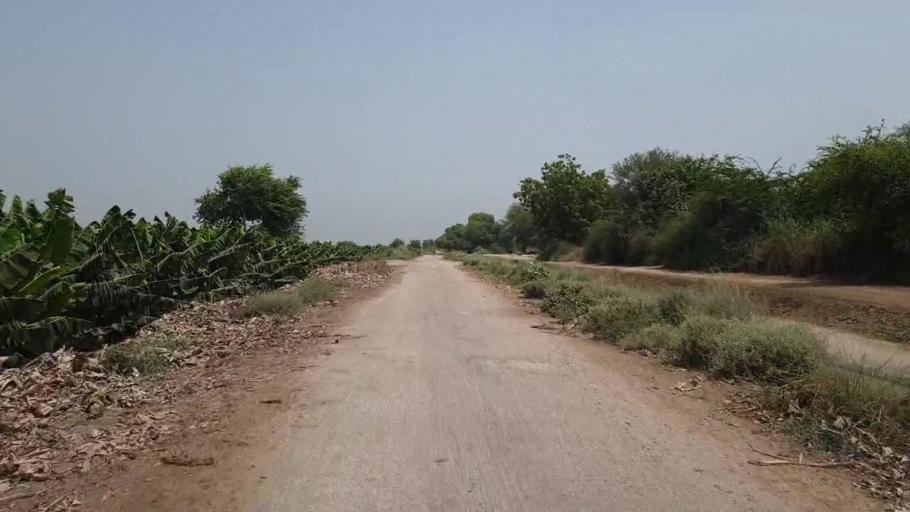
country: PK
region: Sindh
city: Nawabshah
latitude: 26.2863
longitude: 68.3100
